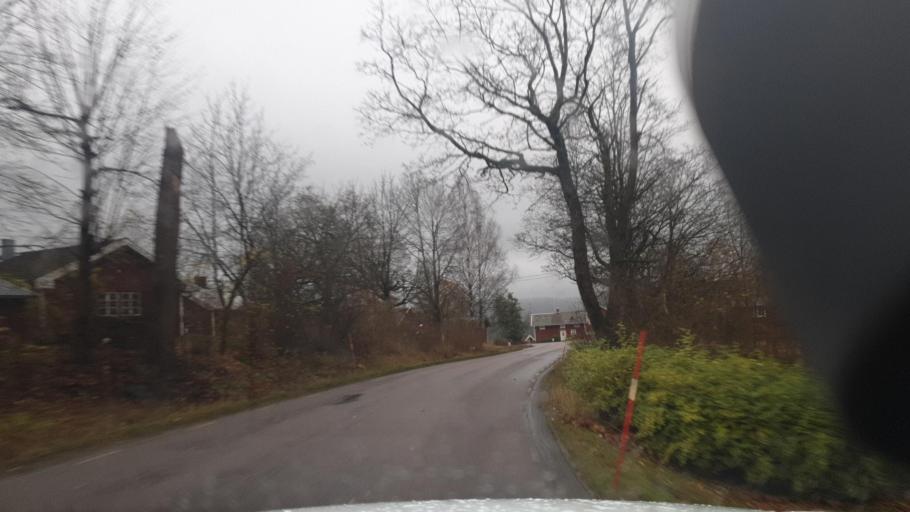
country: SE
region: Vaermland
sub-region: Eda Kommun
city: Charlottenberg
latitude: 59.7472
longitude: 12.1631
